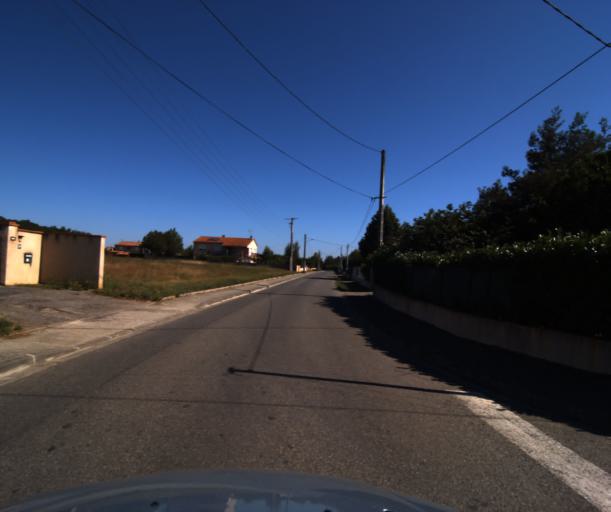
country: FR
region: Midi-Pyrenees
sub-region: Departement de la Haute-Garonne
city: Eaunes
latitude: 43.4231
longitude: 1.3481
